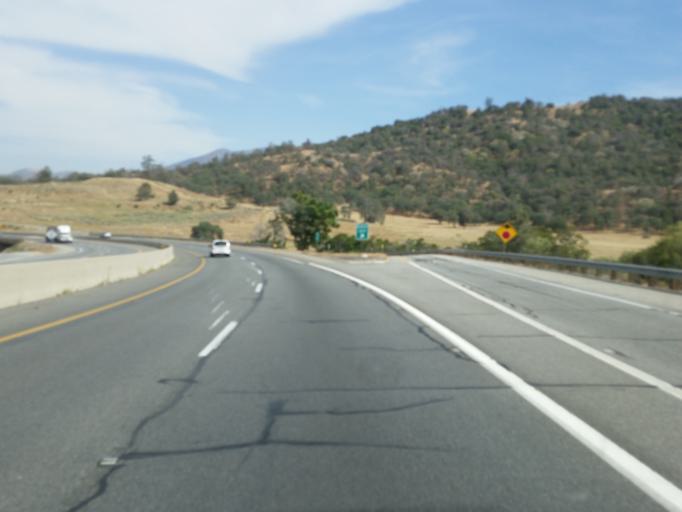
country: US
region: California
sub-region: Kern County
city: Bear Valley Springs
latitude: 35.2424
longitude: -118.5891
